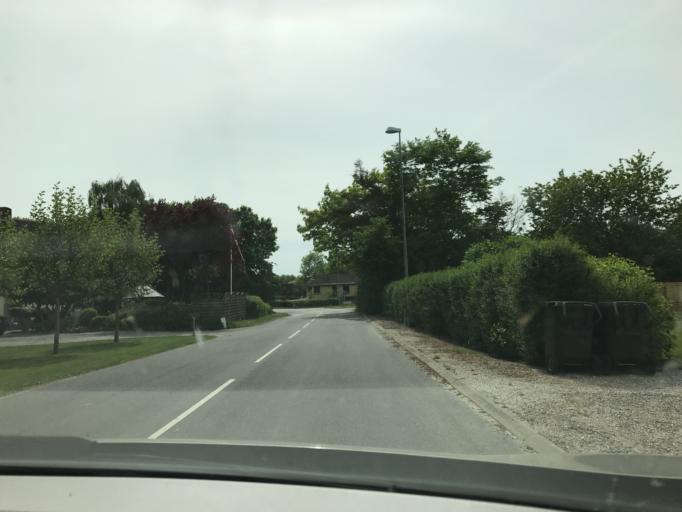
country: DK
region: Central Jutland
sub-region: Norddjurs Kommune
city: Allingabro
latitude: 56.5549
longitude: 10.3001
